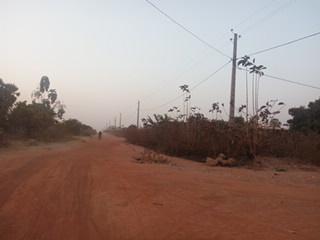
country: BJ
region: Borgou
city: Parakou
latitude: 9.3205
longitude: 2.5970
